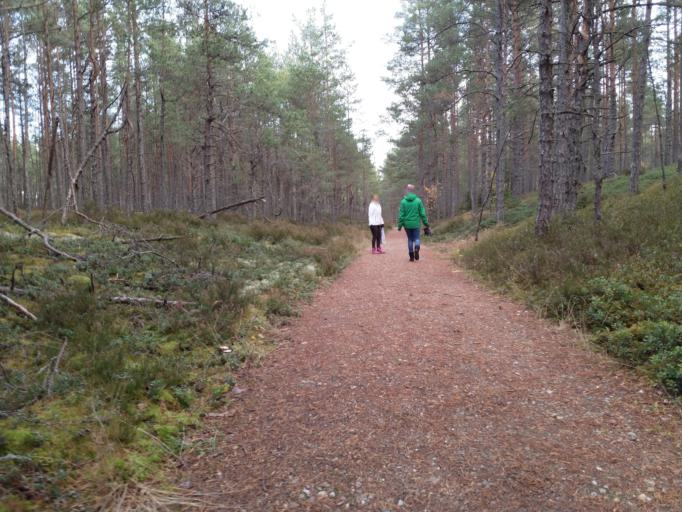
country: LV
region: Dundaga
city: Dundaga
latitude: 57.6513
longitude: 22.2598
